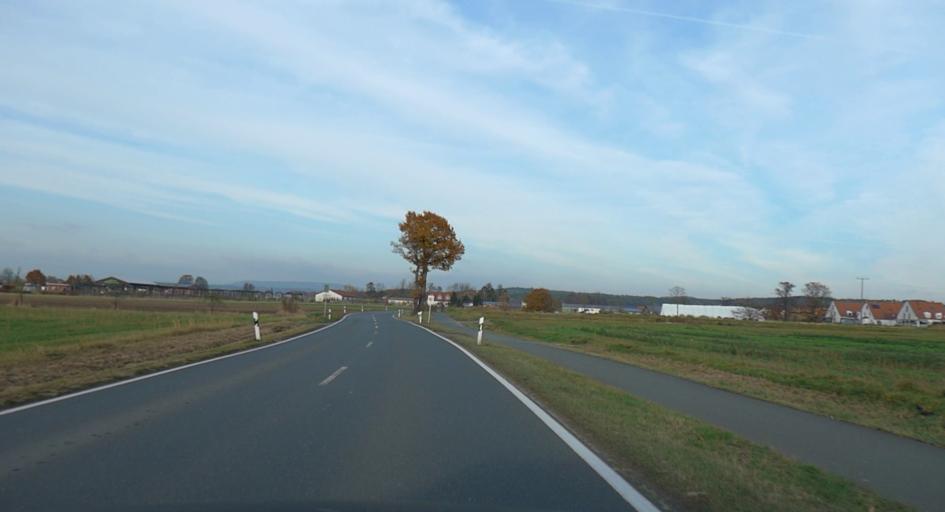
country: DE
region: Bavaria
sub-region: Upper Franconia
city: Poxdorf
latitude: 49.6609
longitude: 11.0600
